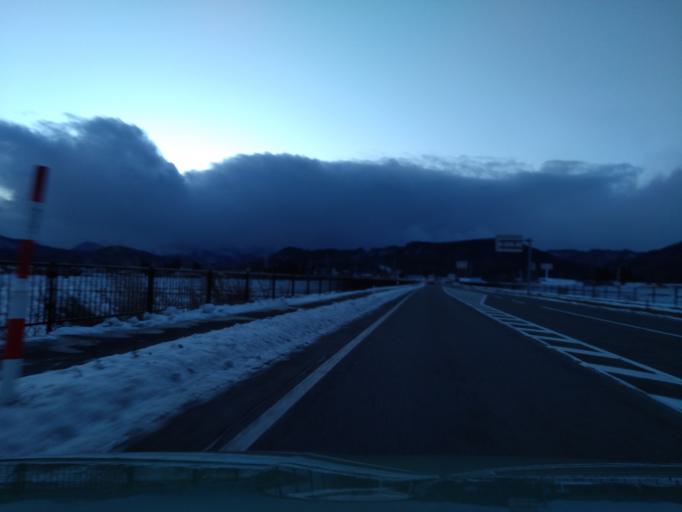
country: JP
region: Iwate
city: Shizukuishi
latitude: 39.6976
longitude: 140.9471
